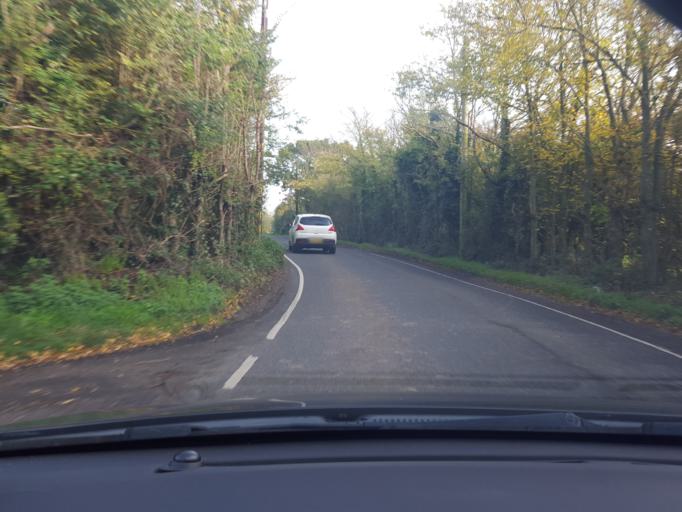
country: GB
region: England
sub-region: Essex
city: Frinton-on-Sea
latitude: 51.8576
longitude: 1.2031
